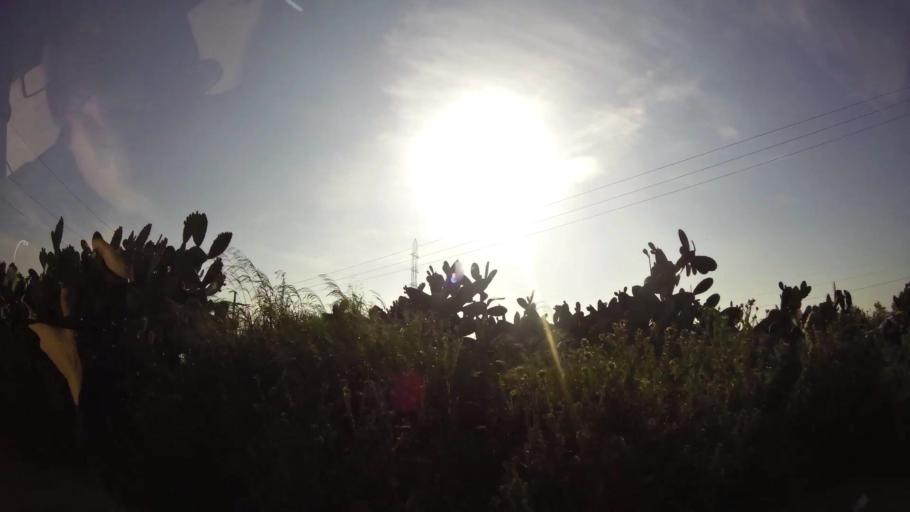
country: MA
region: Oriental
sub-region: Oujda-Angad
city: Oujda
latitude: 34.7191
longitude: -1.9053
